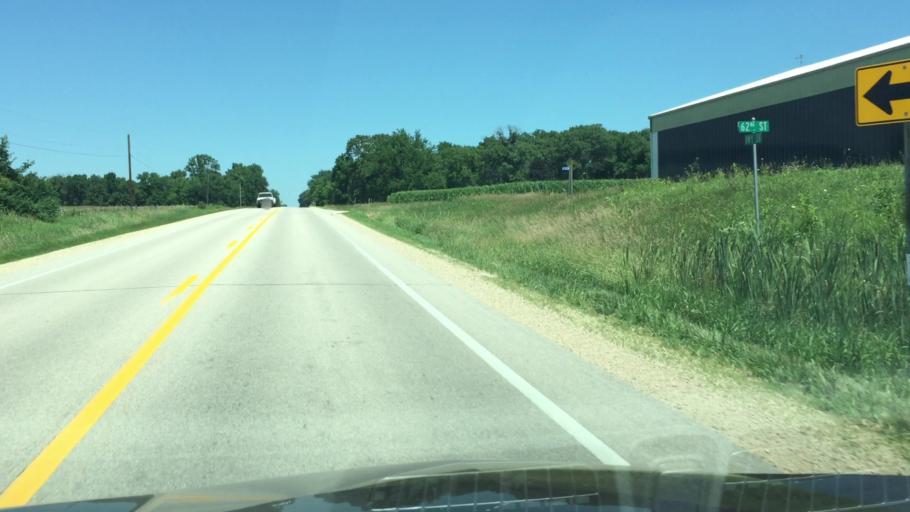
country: US
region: Iowa
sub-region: Cedar County
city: Mechanicsville
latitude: 42.0234
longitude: -91.1367
